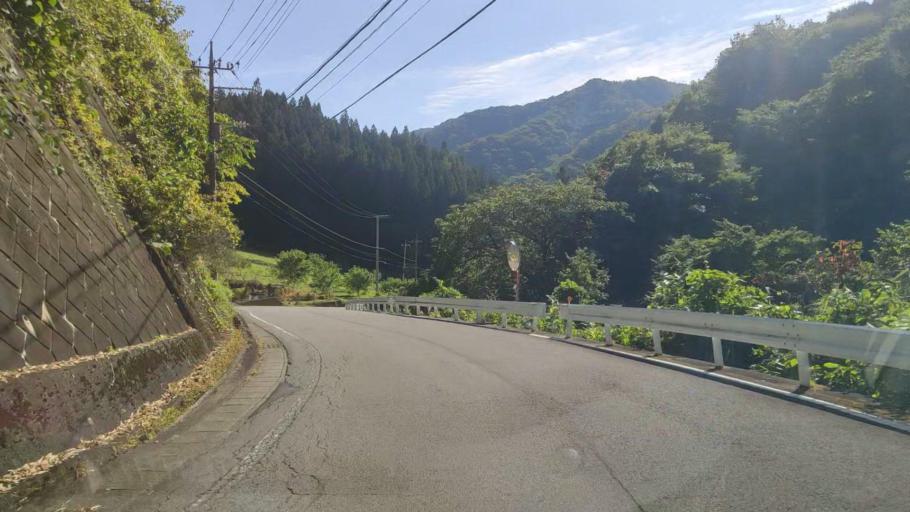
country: JP
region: Gunma
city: Nakanojomachi
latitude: 36.5998
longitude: 138.7067
